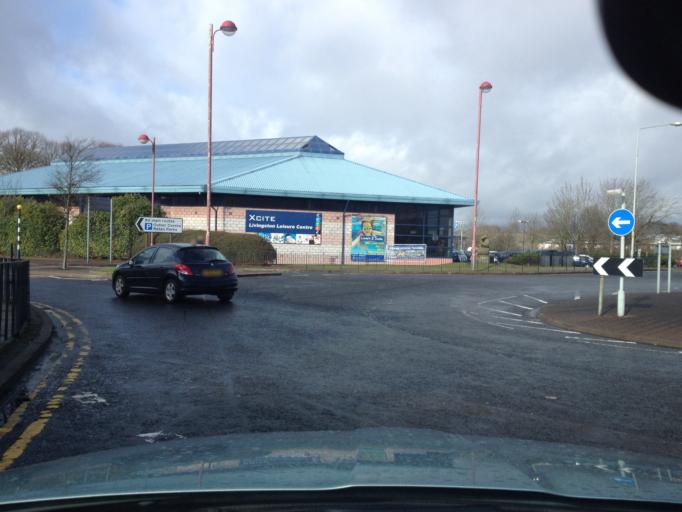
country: GB
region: Scotland
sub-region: West Lothian
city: Livingston
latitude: 55.8840
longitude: -3.5186
